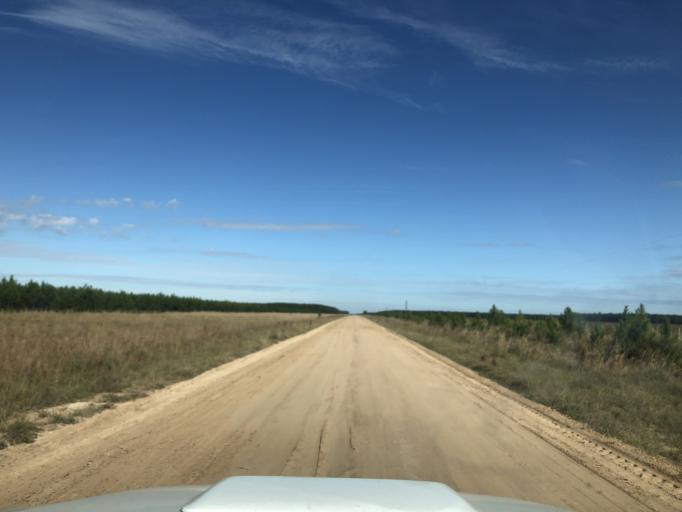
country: AR
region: Corrientes
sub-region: Departamento de Concepcion
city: Concepcion
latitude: -28.5479
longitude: -58.1112
